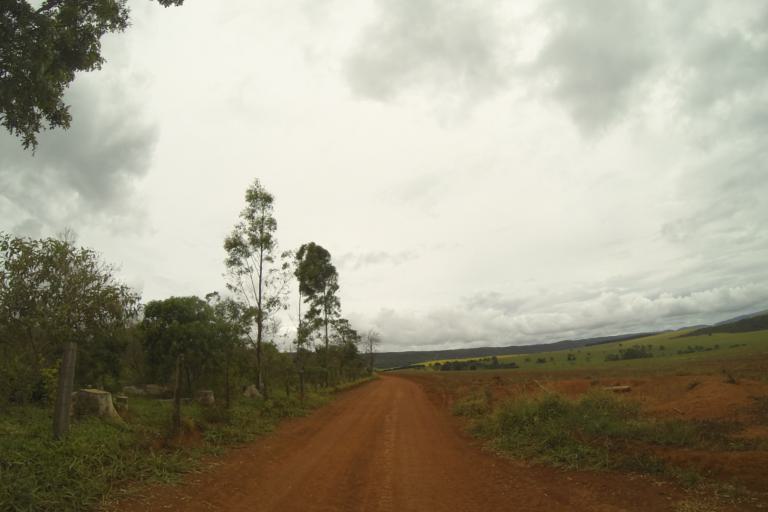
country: BR
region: Minas Gerais
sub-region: Ibia
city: Ibia
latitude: -19.7371
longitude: -46.6105
